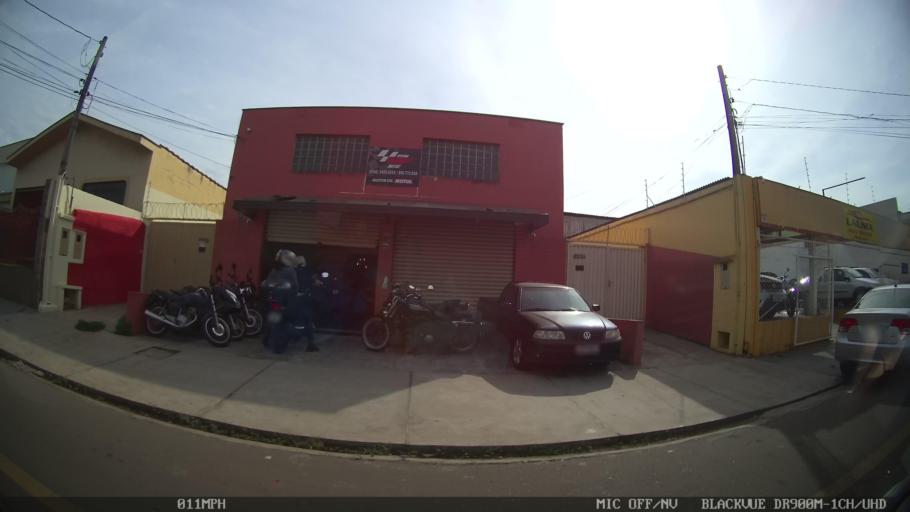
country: BR
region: Sao Paulo
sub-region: Piracicaba
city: Piracicaba
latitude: -22.7384
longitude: -47.6520
